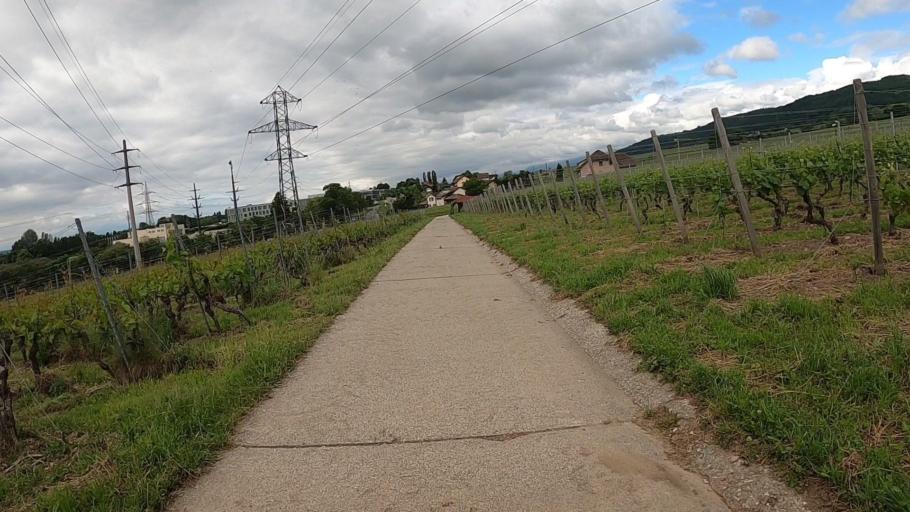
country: CH
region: Vaud
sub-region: Nyon District
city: Rolle
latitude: 46.4641
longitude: 6.3286
